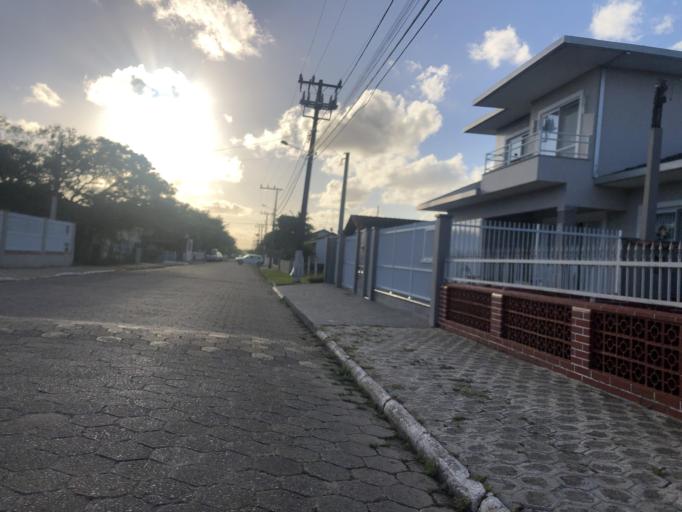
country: BR
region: Santa Catarina
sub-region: Sao Francisco Do Sul
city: Sao Francisco do Sul
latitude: -26.2169
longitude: -48.5248
